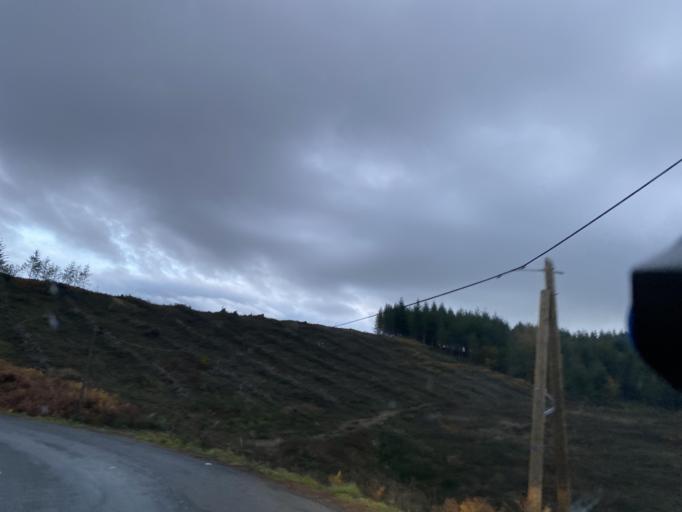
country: FR
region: Auvergne
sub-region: Departement du Puy-de-Dome
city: Celles-sur-Durolle
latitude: 45.8431
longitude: 3.6311
